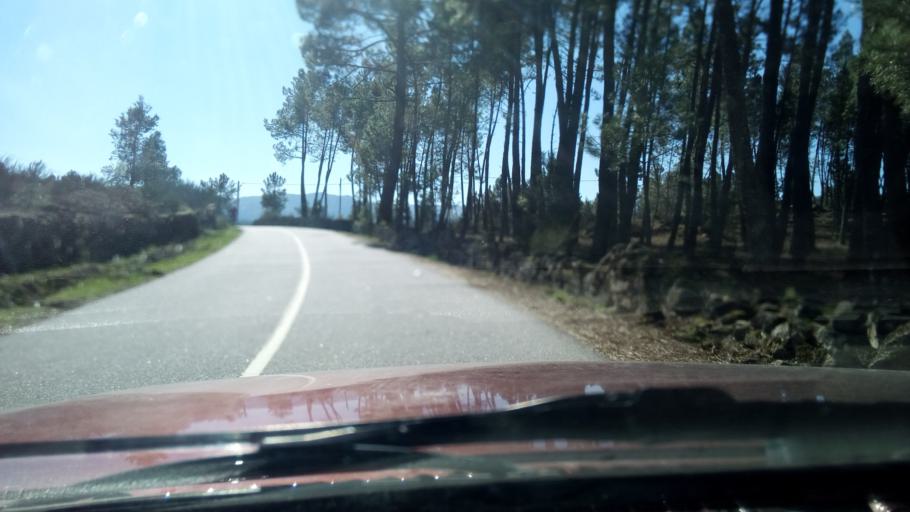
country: PT
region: Guarda
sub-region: Fornos de Algodres
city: Fornos de Algodres
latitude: 40.5913
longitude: -7.5104
